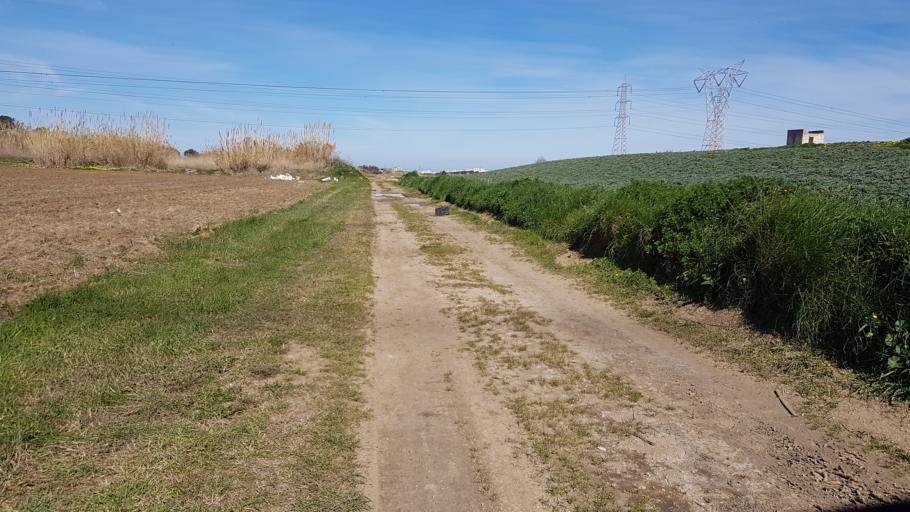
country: IT
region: Apulia
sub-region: Provincia di Brindisi
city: La Rosa
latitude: 40.5969
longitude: 17.9275
